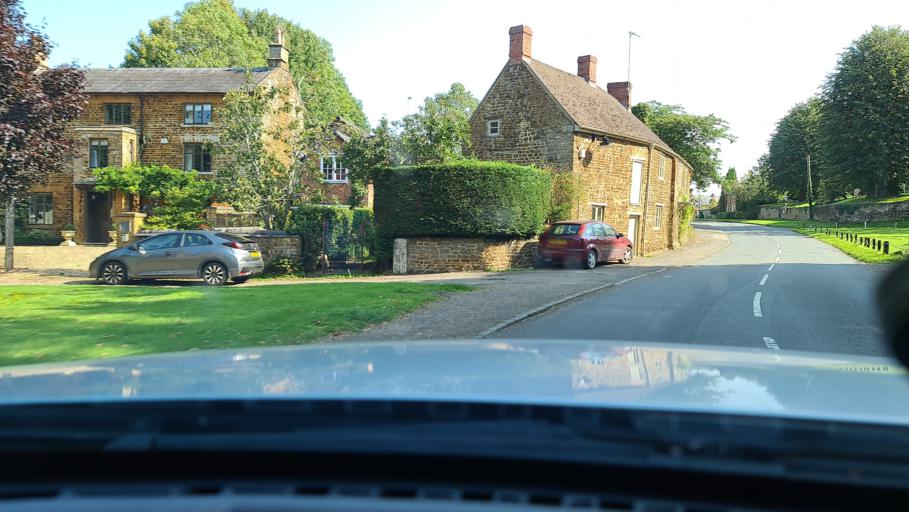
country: GB
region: England
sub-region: Northamptonshire
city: Bugbrooke
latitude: 52.1831
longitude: -1.0775
